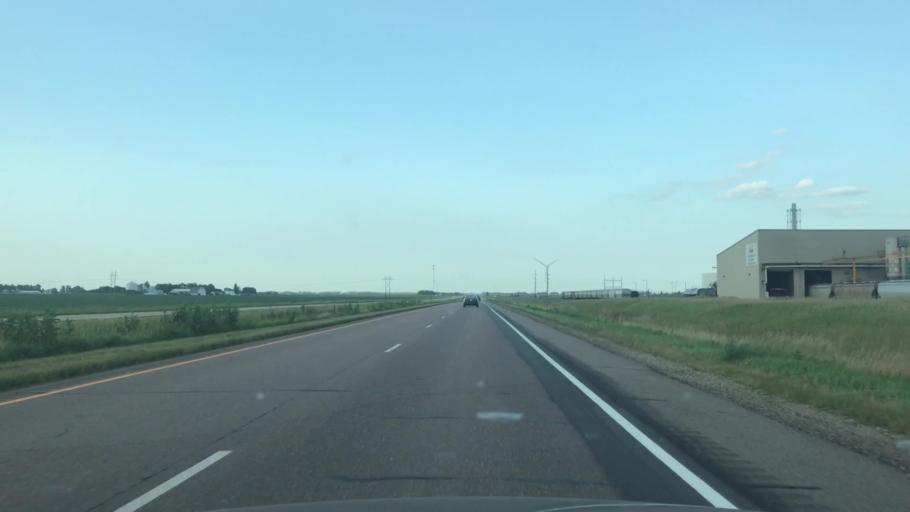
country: US
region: Minnesota
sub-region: Nobles County
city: Worthington
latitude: 43.7056
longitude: -95.4607
